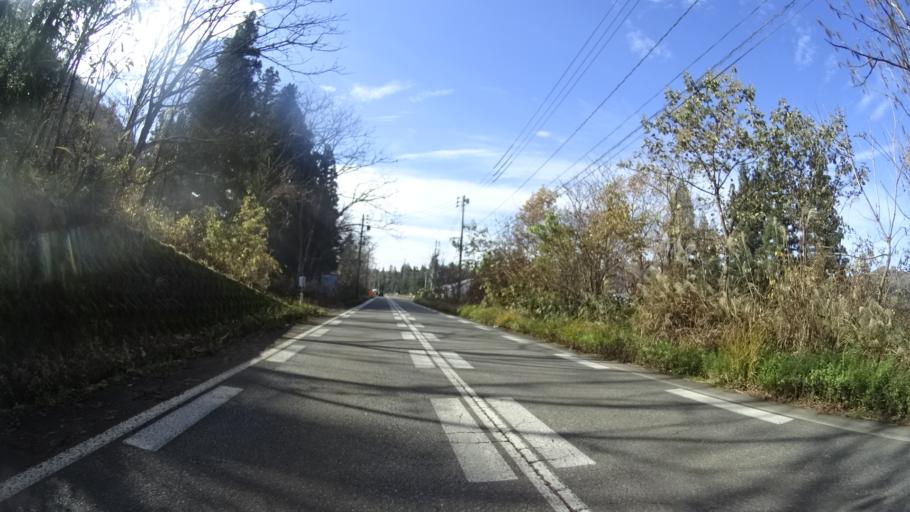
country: JP
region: Niigata
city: Ojiya
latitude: 37.2733
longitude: 138.9899
